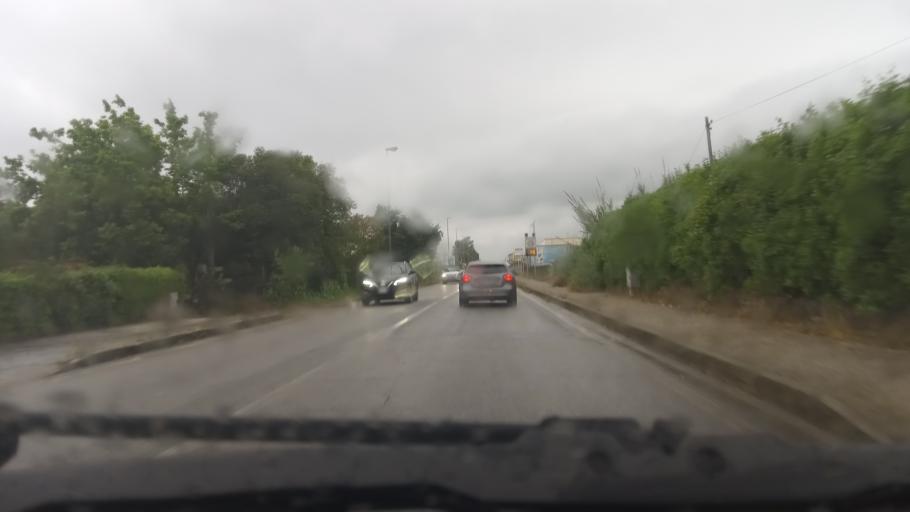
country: IT
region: Latium
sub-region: Provincia di Latina
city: Penitro
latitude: 41.2642
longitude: 13.6750
